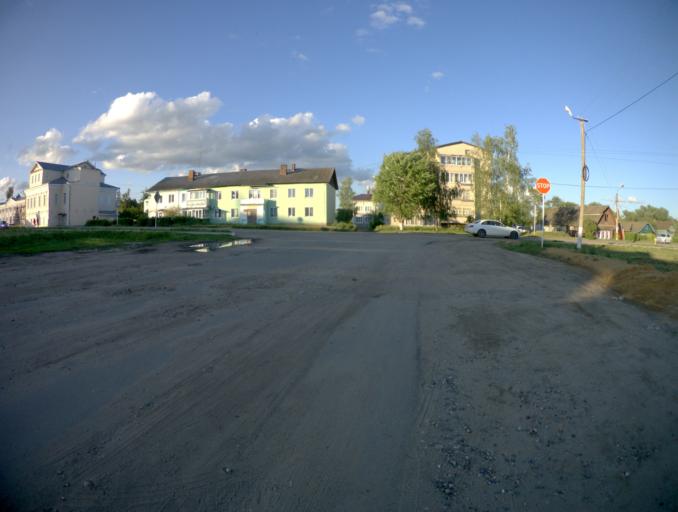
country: RU
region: Ivanovo
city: Gavrilov Posad
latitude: 56.5579
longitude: 40.1226
